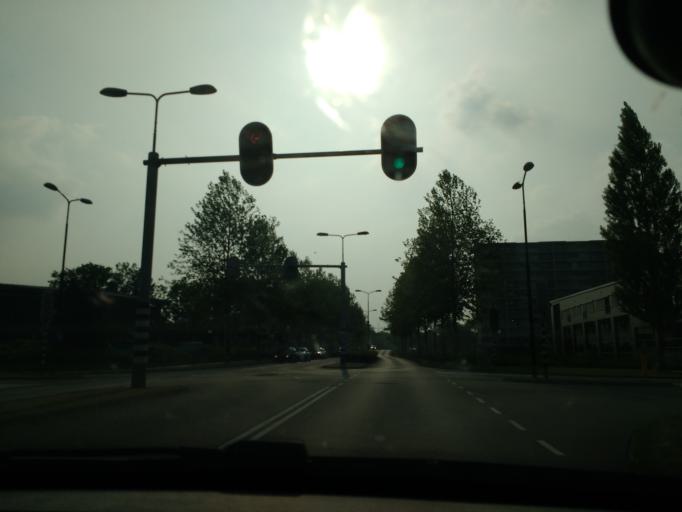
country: NL
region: Utrecht
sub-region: Gemeente Veenendaal
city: Veenendaal
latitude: 52.0223
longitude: 5.5721
